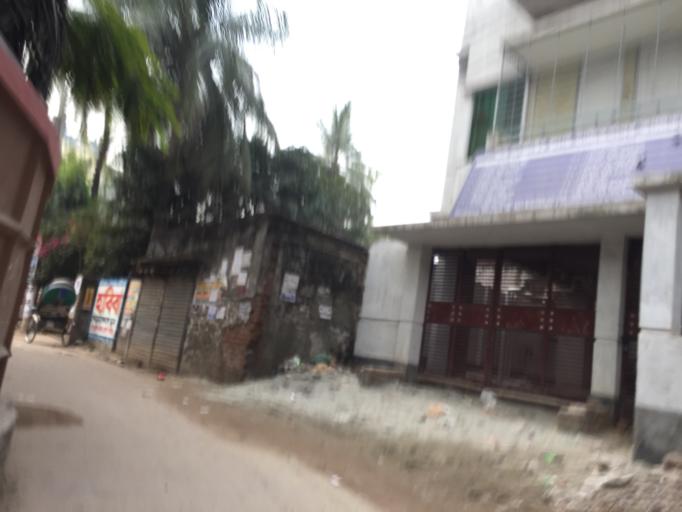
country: BD
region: Dhaka
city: Azimpur
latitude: 23.7976
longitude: 90.3627
